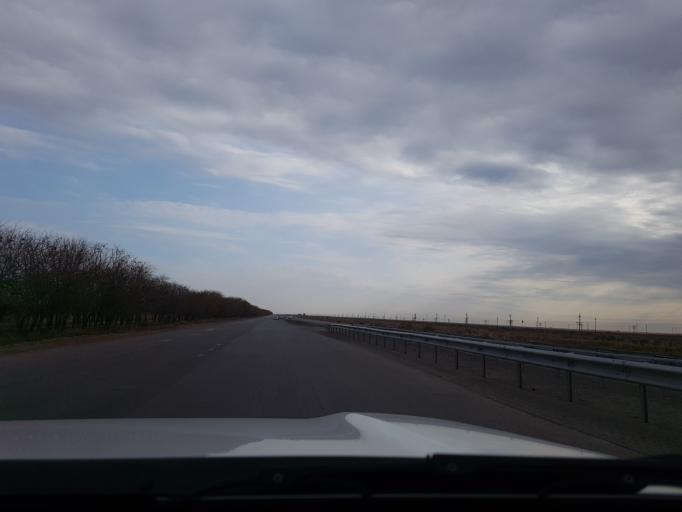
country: TM
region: Ahal
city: Tejen
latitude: 37.2387
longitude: 60.1681
